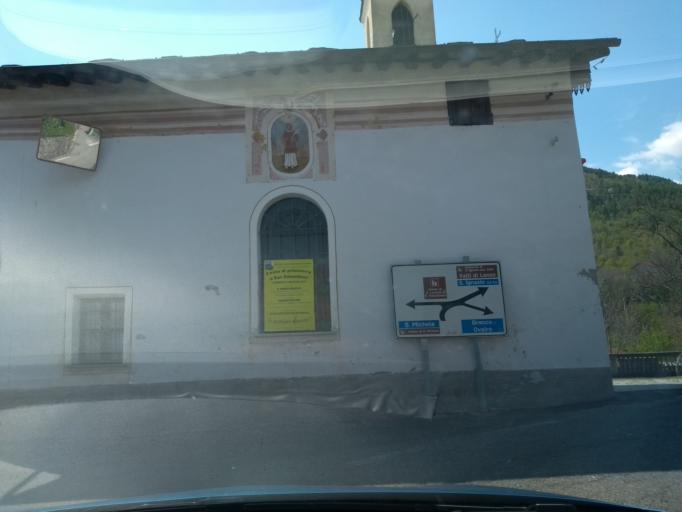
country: IT
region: Piedmont
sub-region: Provincia di Torino
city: Lanzo Torinese
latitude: 45.2794
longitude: 7.4679
